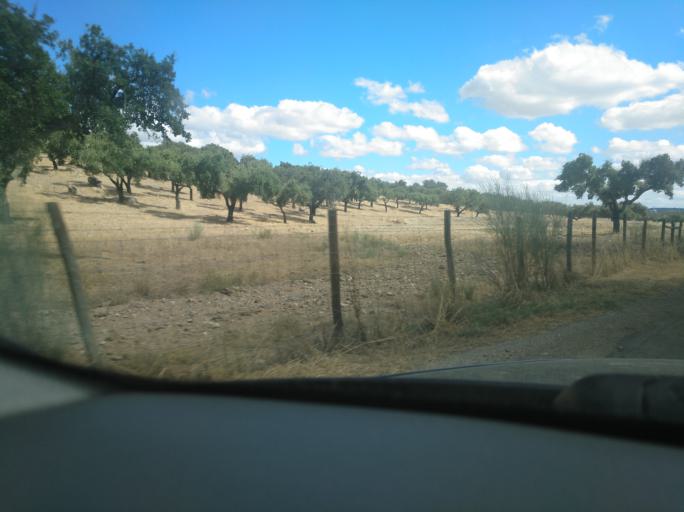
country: ES
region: Extremadura
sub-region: Provincia de Badajoz
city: La Codosera
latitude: 39.1418
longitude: -7.1569
